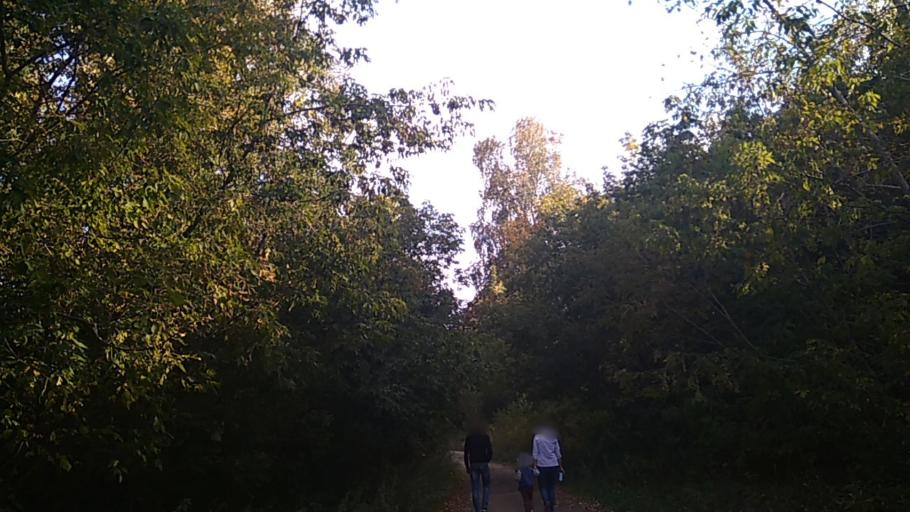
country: RU
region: Sverdlovsk
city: Pokrovskoye
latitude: 56.4350
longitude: 61.5930
